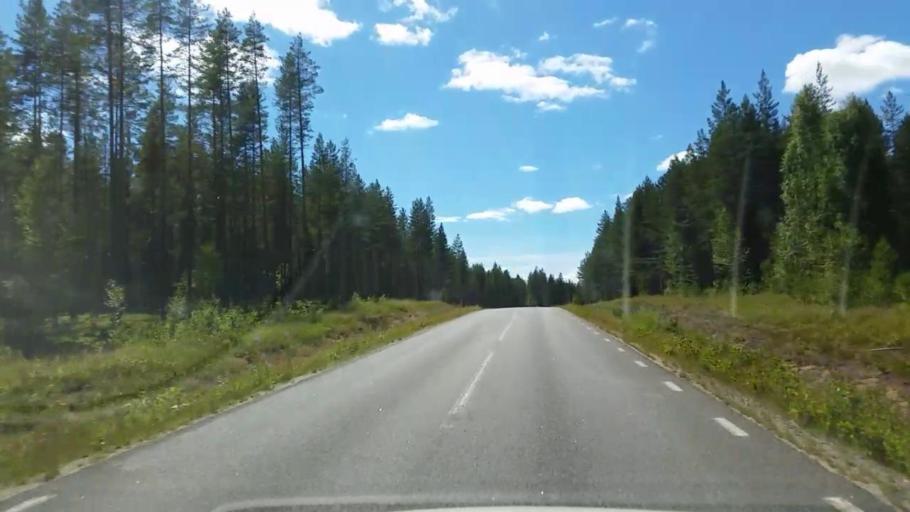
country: SE
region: Gaevleborg
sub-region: Ljusdals Kommun
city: Farila
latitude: 61.7536
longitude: 15.7720
